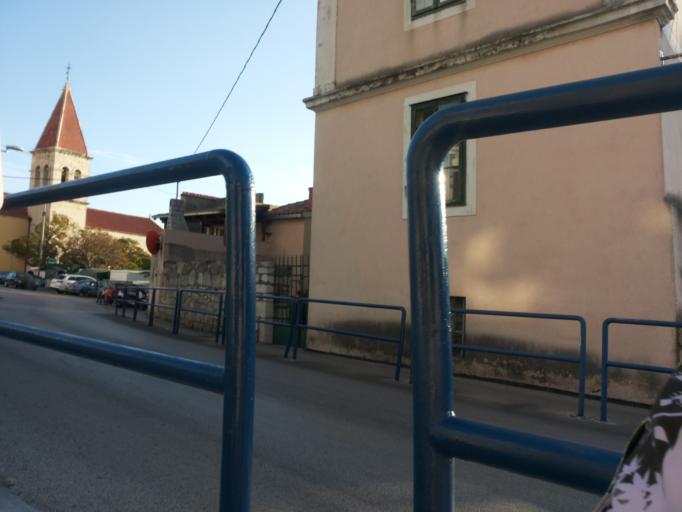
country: HR
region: Splitsko-Dalmatinska
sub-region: Grad Makarska
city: Makarska
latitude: 43.2948
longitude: 17.0211
